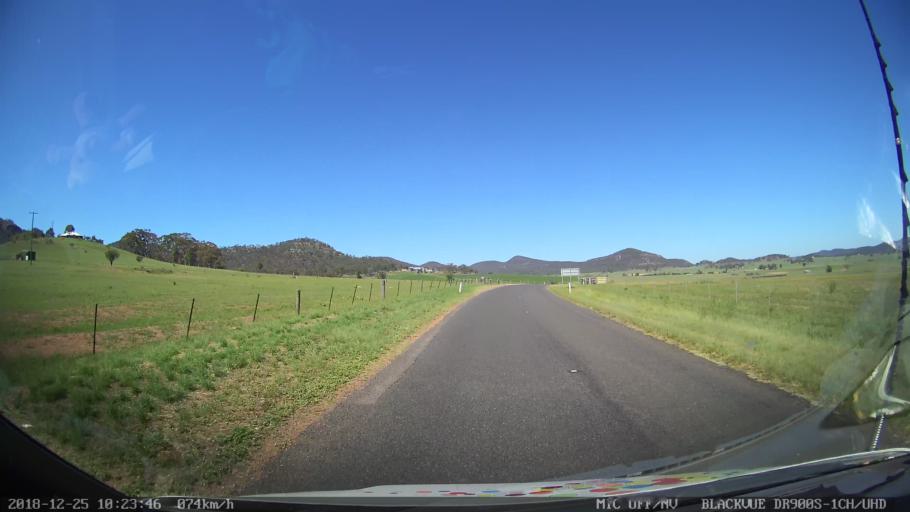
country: AU
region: New South Wales
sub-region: Muswellbrook
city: Denman
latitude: -32.3890
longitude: 150.5209
